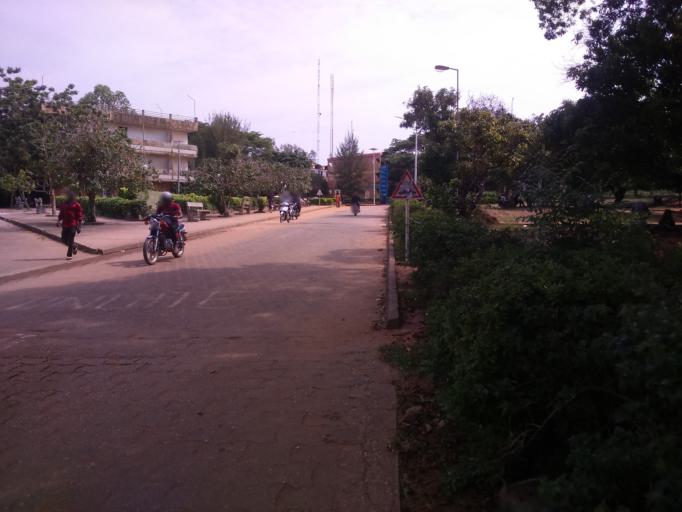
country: BJ
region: Atlantique
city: Abomey-Calavi
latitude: 6.4138
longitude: 2.3438
